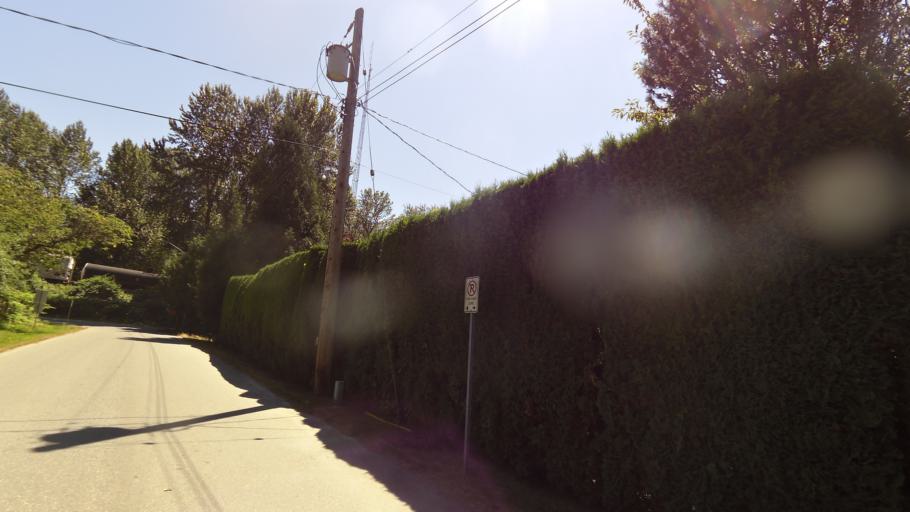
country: CA
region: British Columbia
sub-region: Fraser Valley Regional District
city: Chilliwack
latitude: 49.2361
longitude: -121.9579
